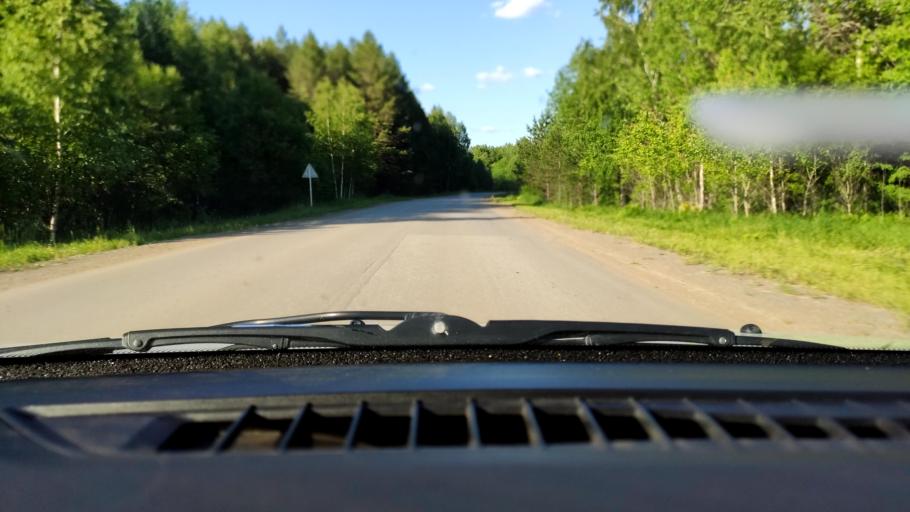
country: RU
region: Perm
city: Orda
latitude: 57.1222
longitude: 56.6764
